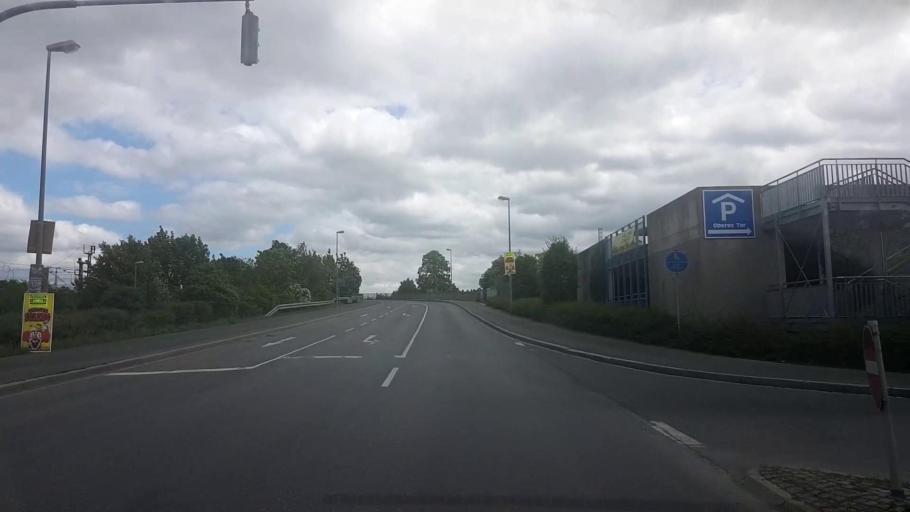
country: DE
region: Bavaria
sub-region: Upper Franconia
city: Lichtenfels
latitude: 50.1482
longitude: 11.0645
